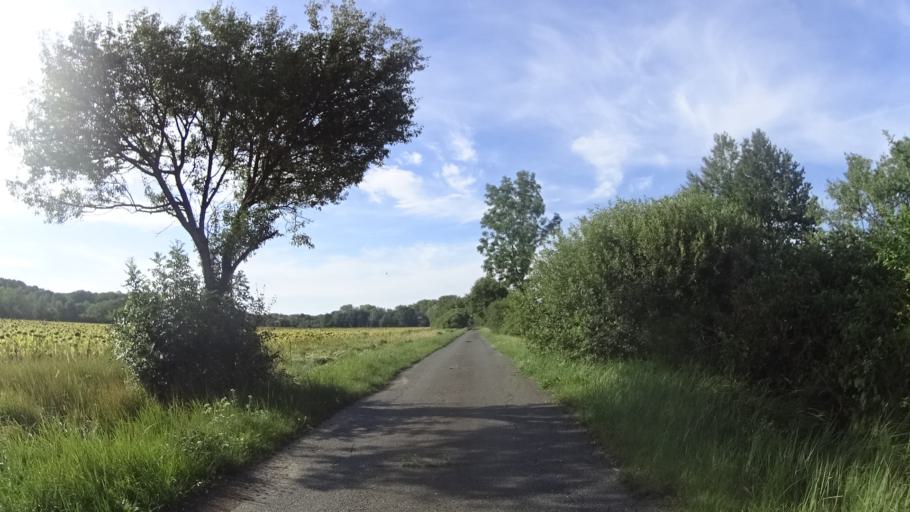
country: AT
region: Lower Austria
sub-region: Politischer Bezirk Ganserndorf
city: Drosing
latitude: 48.5629
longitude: 16.9574
